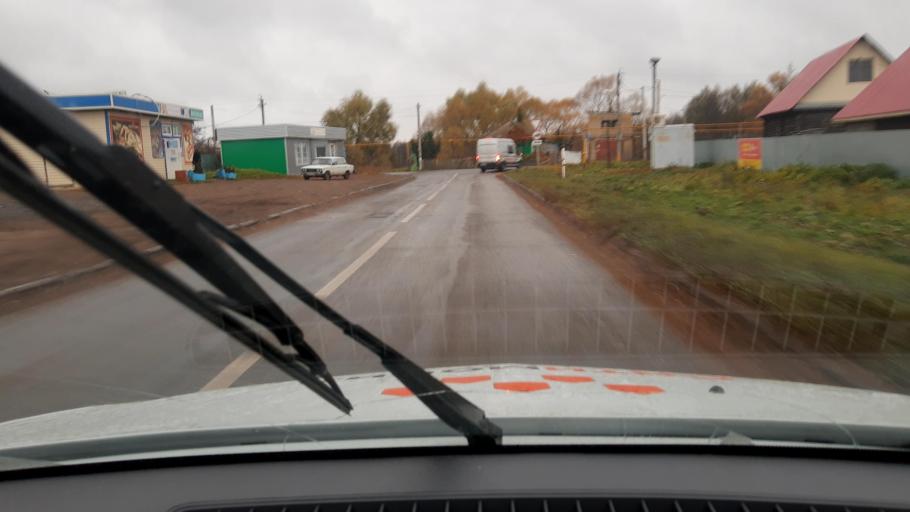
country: RU
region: Bashkortostan
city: Kabakovo
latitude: 54.7452
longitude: 56.1983
